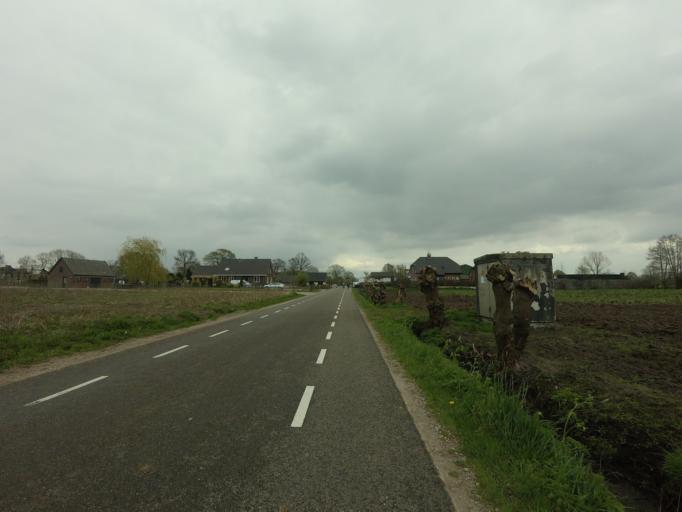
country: NL
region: Gelderland
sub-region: Gemeente Ede
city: Ederveen
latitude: 52.0678
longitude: 5.5700
